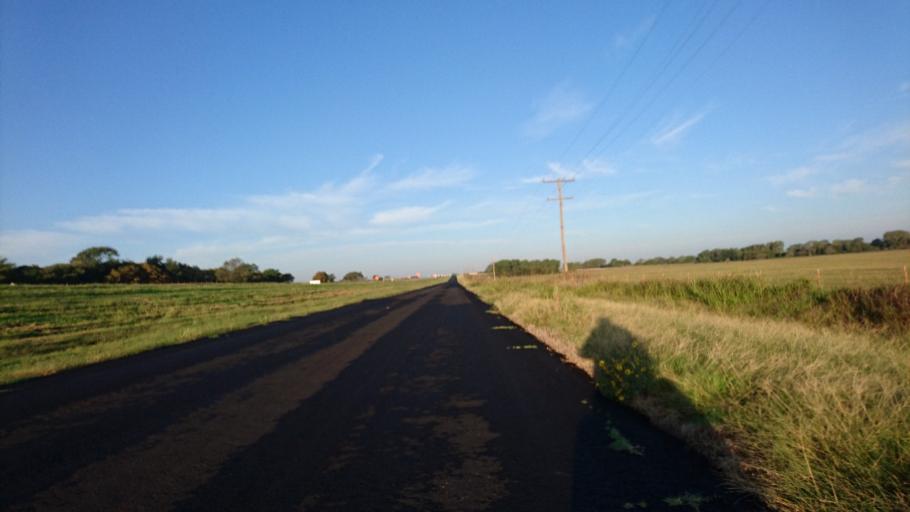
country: US
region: Oklahoma
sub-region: Beckham County
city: Sayre
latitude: 35.2624
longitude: -99.6873
